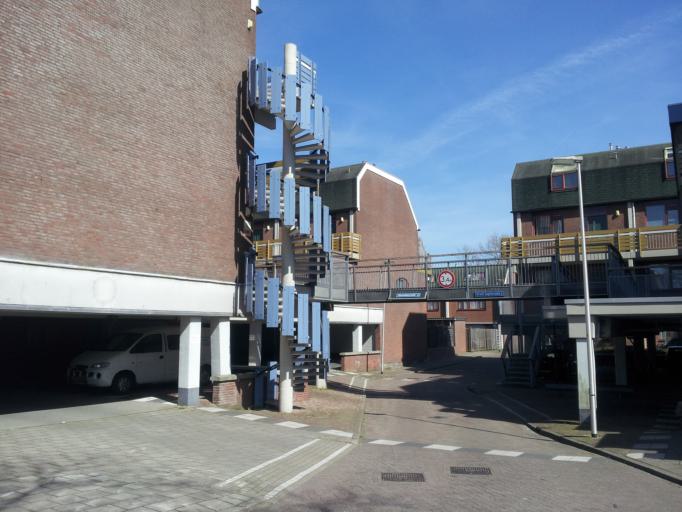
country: NL
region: South Holland
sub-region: Gemeente Zoetermeer
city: Zoetermeer
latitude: 52.0700
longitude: 4.4736
